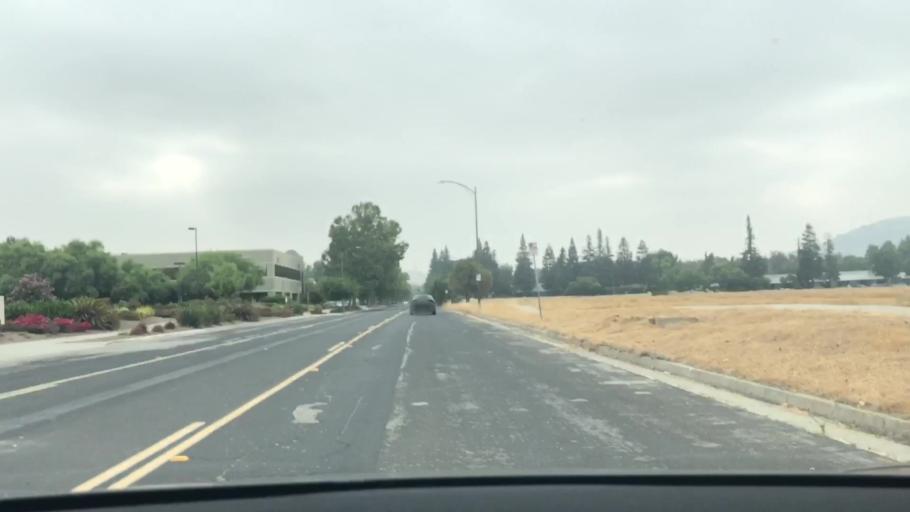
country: US
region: California
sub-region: Santa Clara County
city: Seven Trees
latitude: 37.2349
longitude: -121.7832
